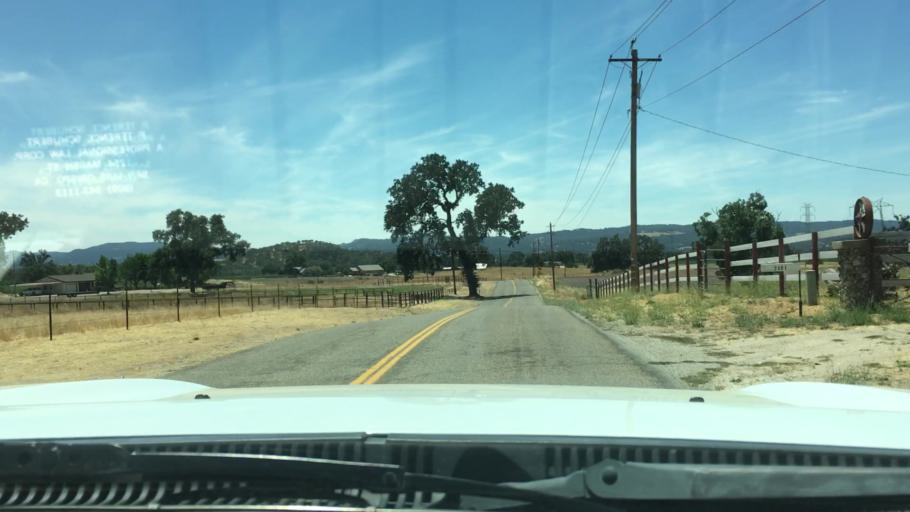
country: US
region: California
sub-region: San Luis Obispo County
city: Templeton
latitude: 35.5680
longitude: -120.6660
